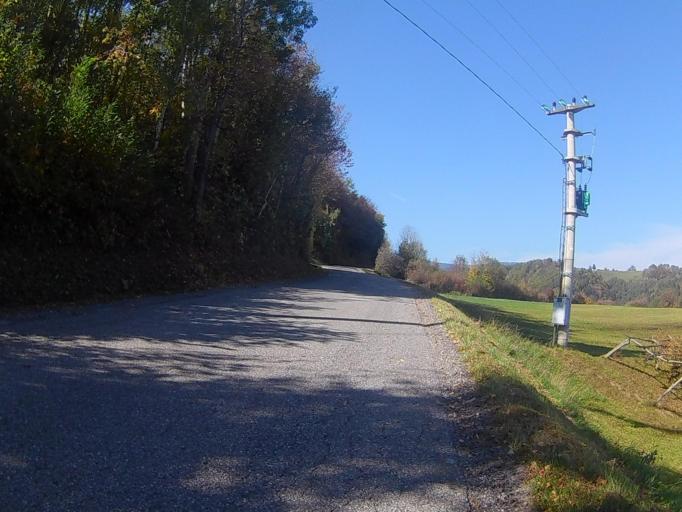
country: SI
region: Race-Fram
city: Fram
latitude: 46.4597
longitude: 15.6170
